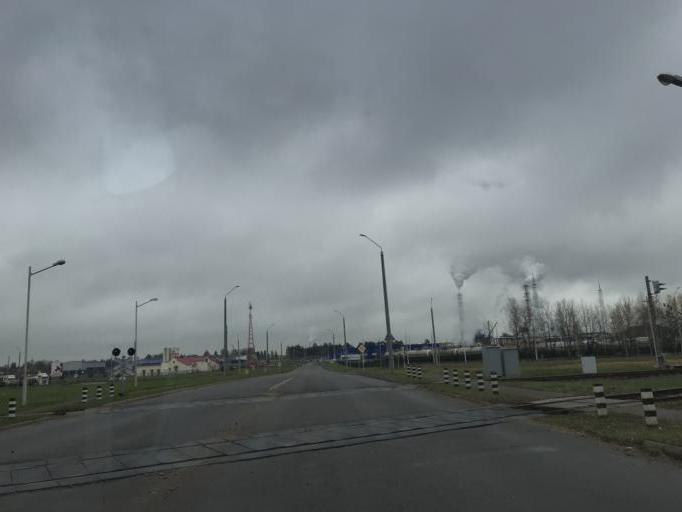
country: BY
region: Mogilev
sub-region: Mahilyowski Rayon
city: Veyno
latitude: 53.8288
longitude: 30.3462
